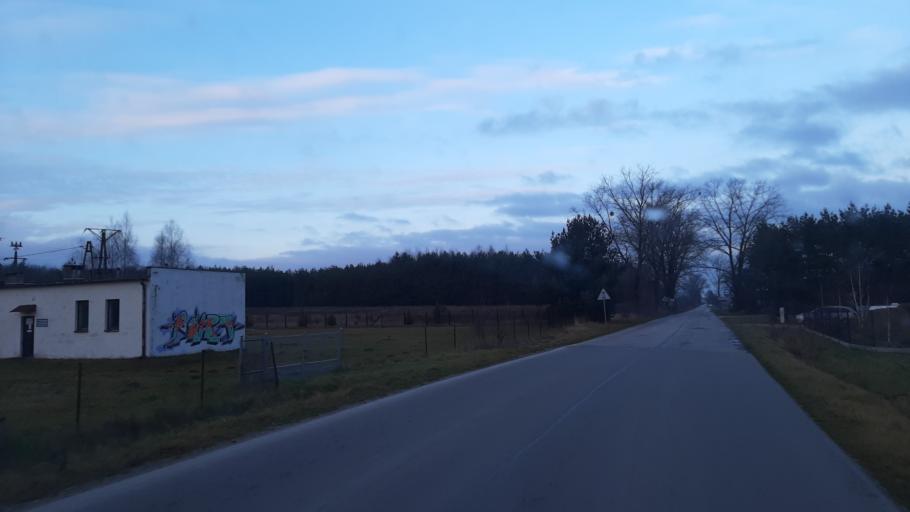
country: PL
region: Lublin Voivodeship
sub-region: Powiat lubelski
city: Garbow
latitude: 51.3949
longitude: 22.4091
